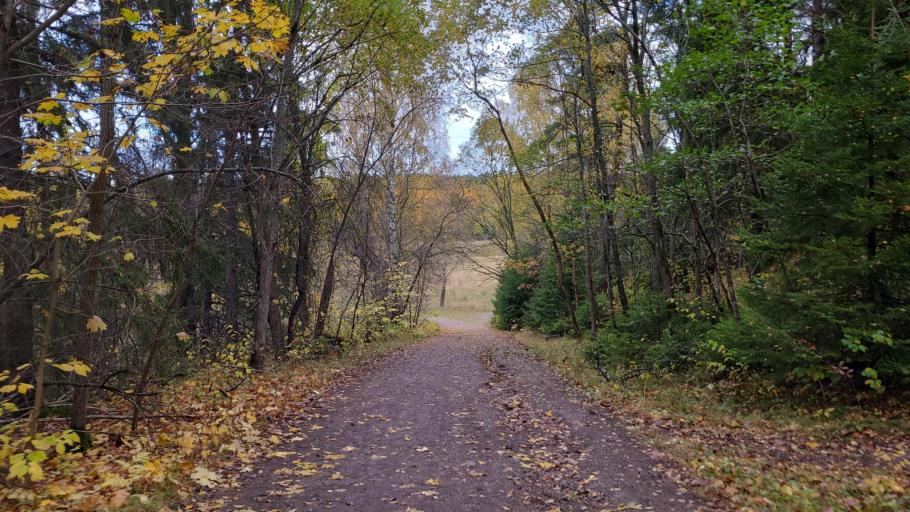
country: SE
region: Stockholm
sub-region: Solna Kommun
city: Rasunda
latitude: 59.3910
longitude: 17.9743
